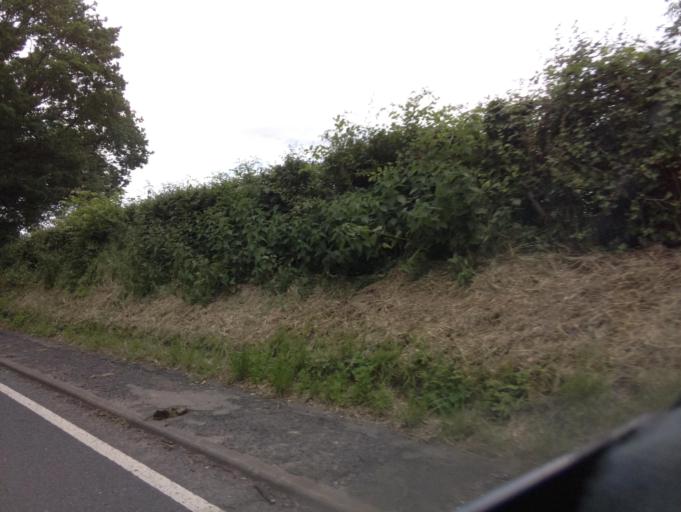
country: GB
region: England
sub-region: Worcestershire
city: Kempsey
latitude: 52.1620
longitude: -2.1612
